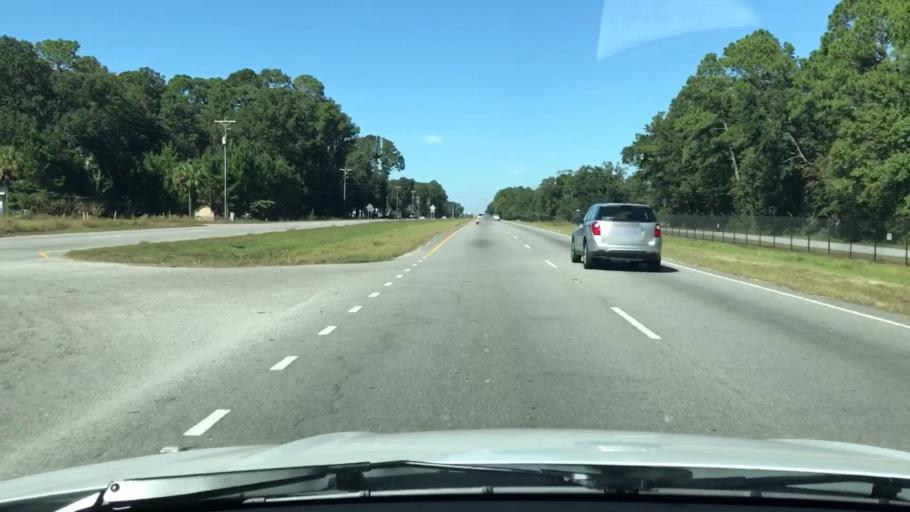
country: US
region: South Carolina
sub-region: Beaufort County
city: Burton
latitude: 32.4850
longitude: -80.7401
